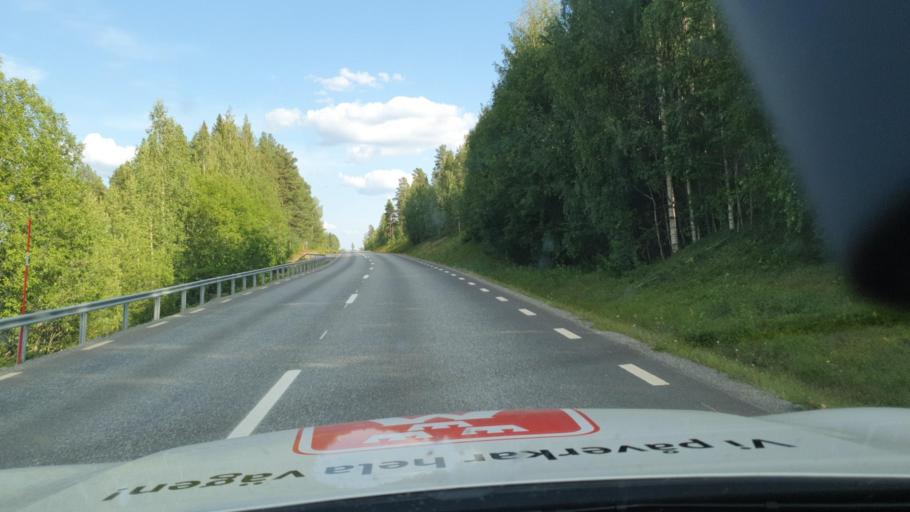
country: SE
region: Vaesterbotten
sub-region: Lycksele Kommun
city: Soderfors
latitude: 64.8413
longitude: 17.9773
